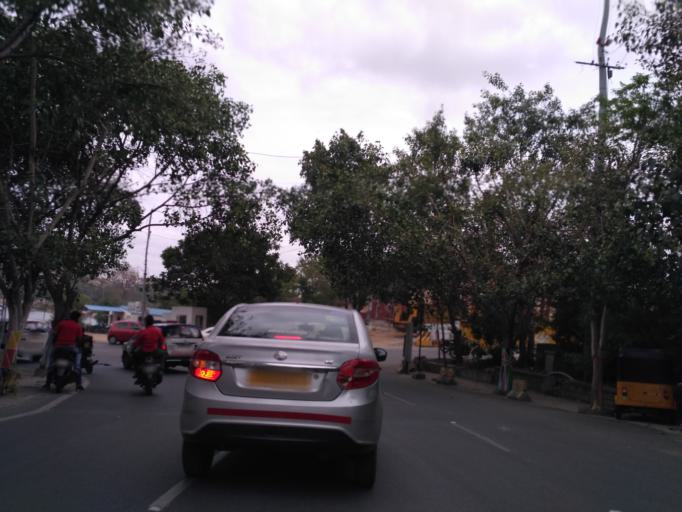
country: IN
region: Telangana
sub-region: Rangareddi
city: Kukatpalli
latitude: 17.4318
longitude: 78.3882
